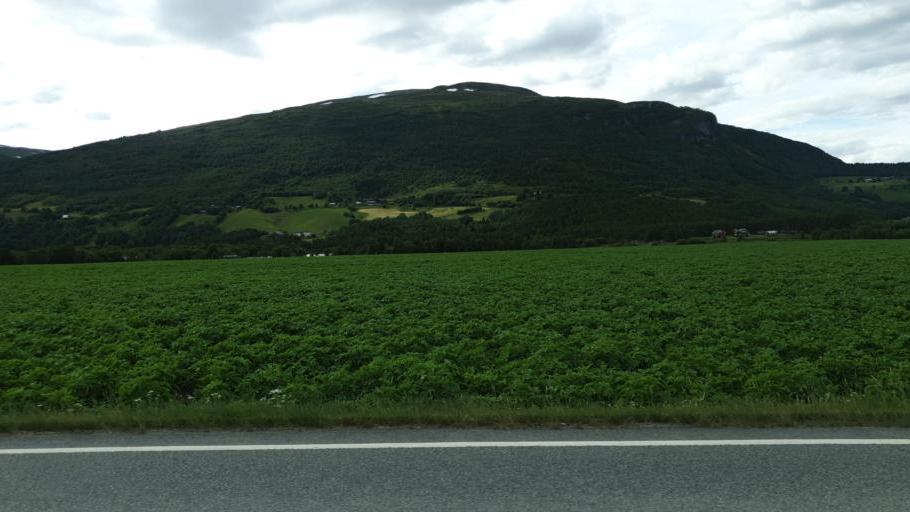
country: NO
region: Sor-Trondelag
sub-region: Oppdal
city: Oppdal
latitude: 62.5384
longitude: 9.6272
